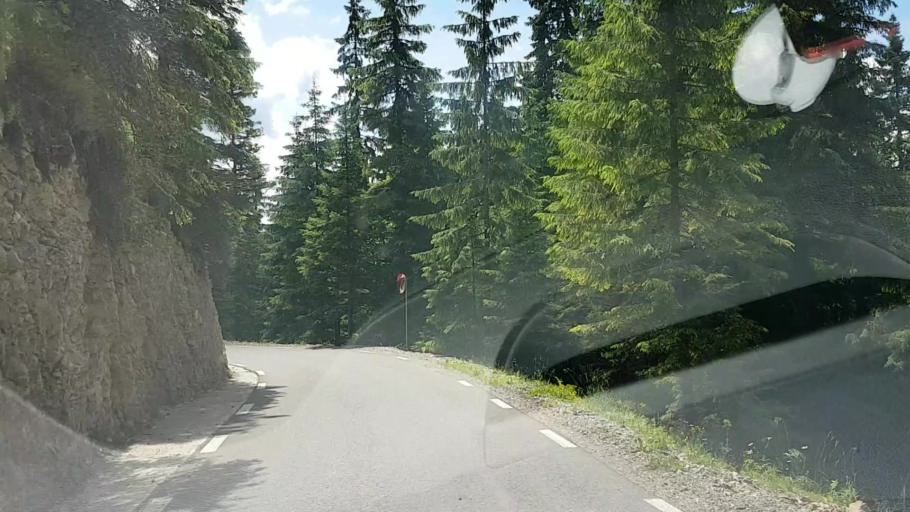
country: RO
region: Suceava
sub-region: Municipiul Campulung Moldovenesc
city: Campulung Moldovenesc
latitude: 47.4498
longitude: 25.5514
